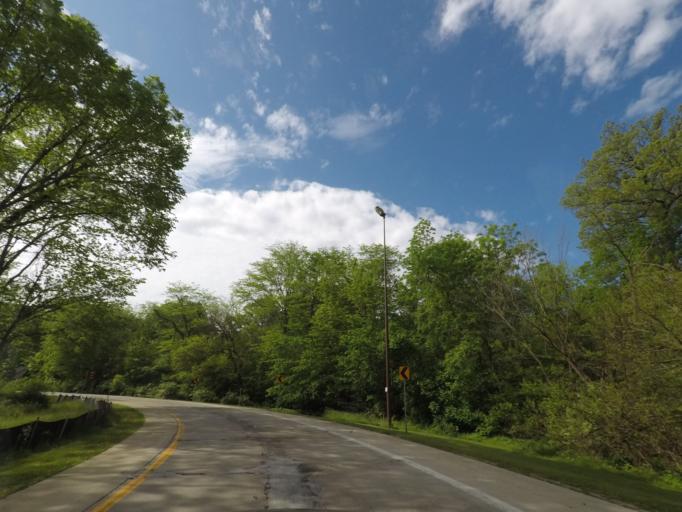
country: US
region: Illinois
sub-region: McLean County
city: Twin Grove
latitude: 40.3604
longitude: -89.1116
